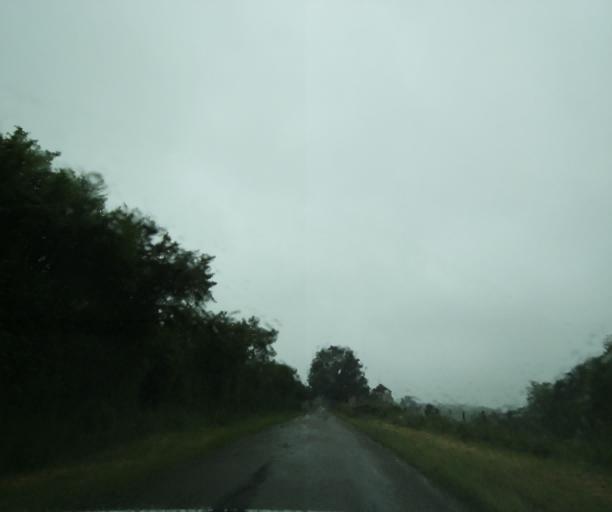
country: FR
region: Bourgogne
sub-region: Departement de Saone-et-Loire
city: Charolles
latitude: 46.4236
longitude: 4.2766
